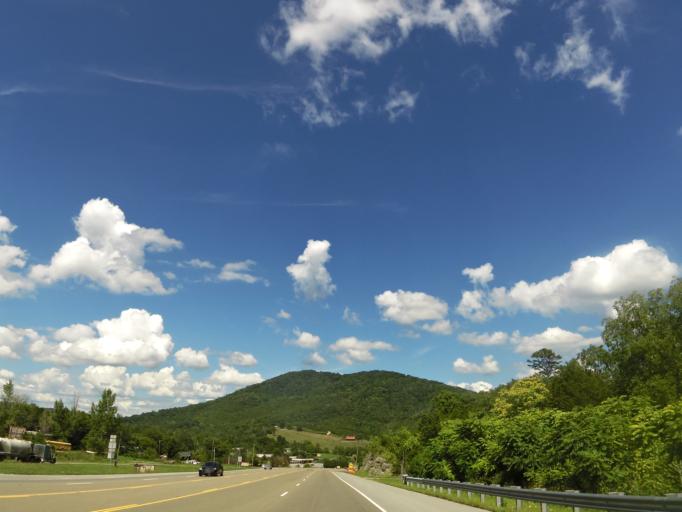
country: US
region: Tennessee
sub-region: Claiborne County
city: Tazewell
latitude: 36.4228
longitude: -83.5313
